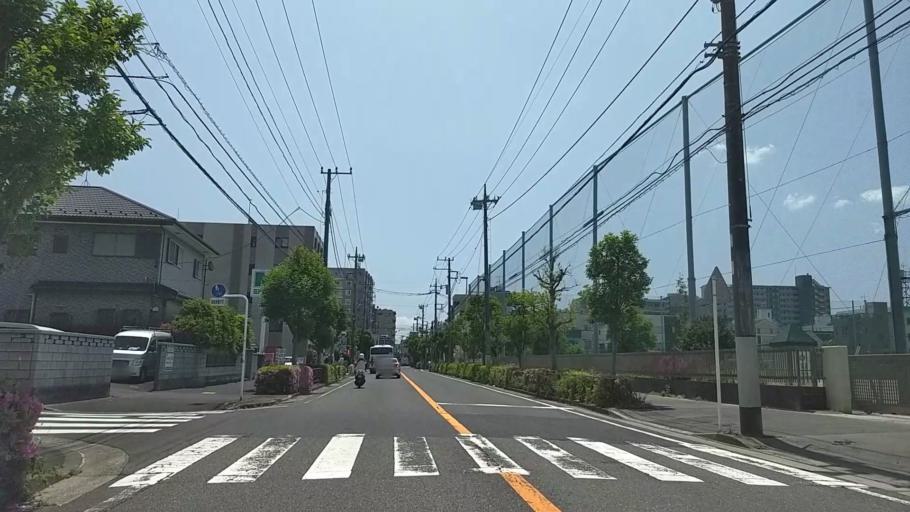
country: JP
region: Kanagawa
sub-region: Kawasaki-shi
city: Kawasaki
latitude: 35.5274
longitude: 139.7229
